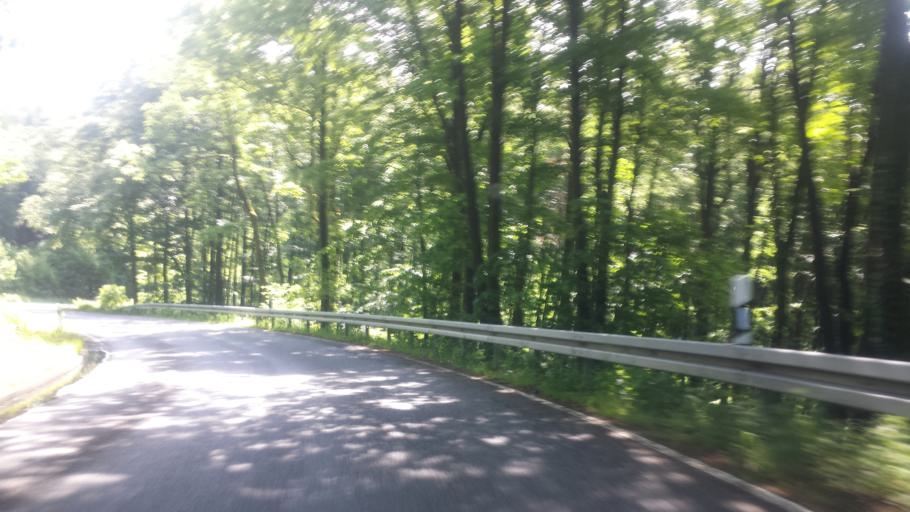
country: DE
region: Hesse
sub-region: Regierungsbezirk Darmstadt
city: Wald-Michelbach
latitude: 49.5734
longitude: 8.8048
